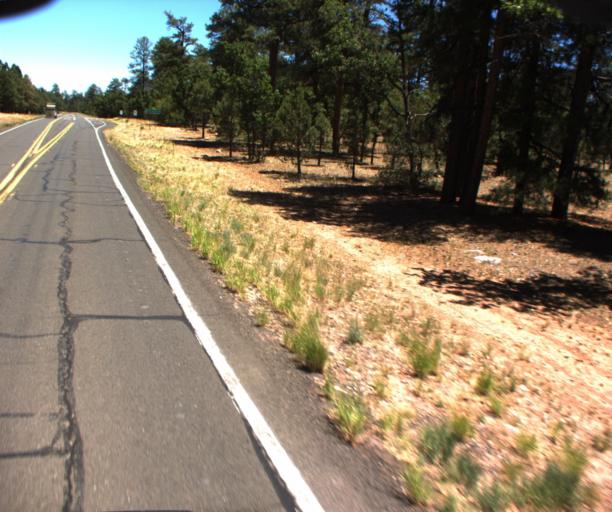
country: US
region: Arizona
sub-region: Gila County
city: Star Valley
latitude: 34.6270
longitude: -111.1293
